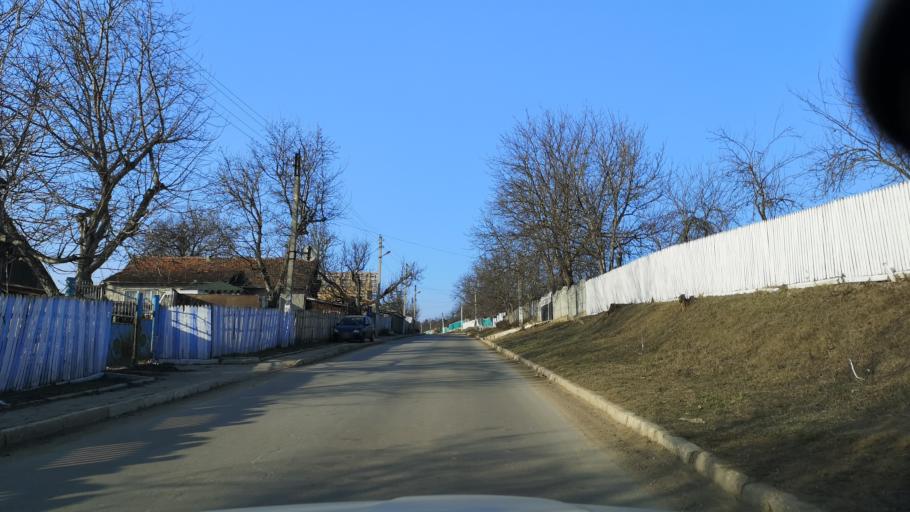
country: MD
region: Stinga Nistrului
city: Bucovat
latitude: 47.1118
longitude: 28.5096
